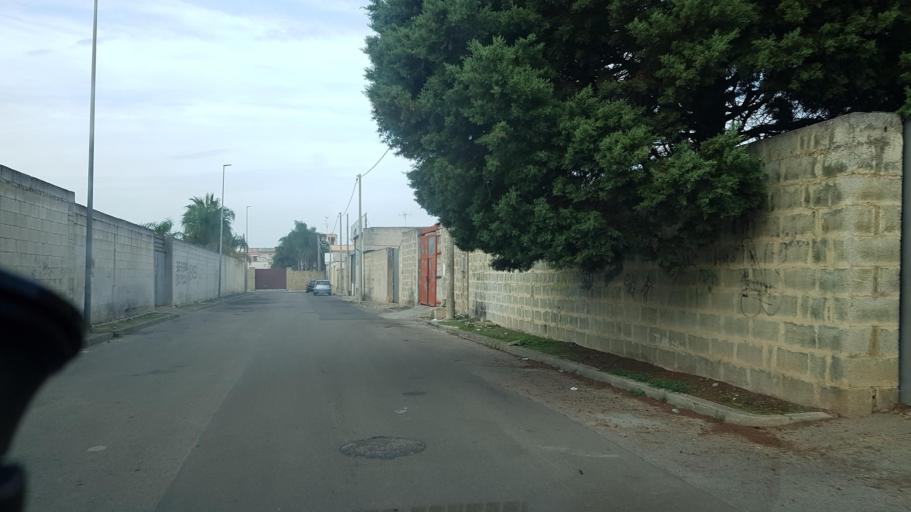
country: IT
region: Apulia
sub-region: Provincia di Lecce
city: Trepuzzi
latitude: 40.4042
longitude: 18.0666
